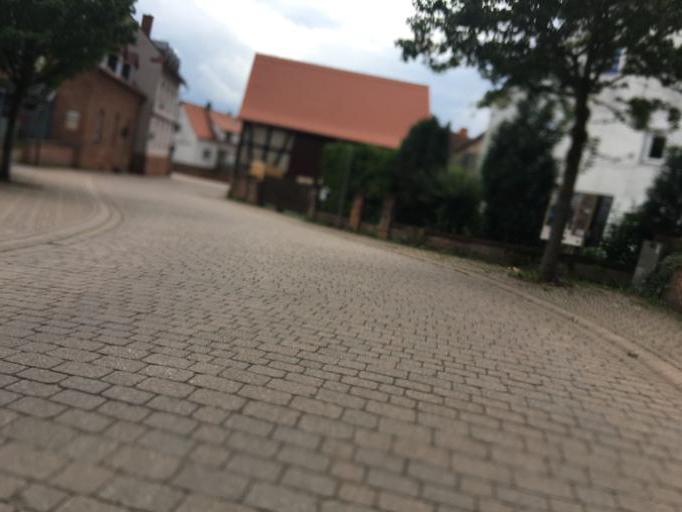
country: DE
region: Hesse
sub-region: Regierungsbezirk Darmstadt
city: Gelnhausen
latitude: 50.1896
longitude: 9.1995
